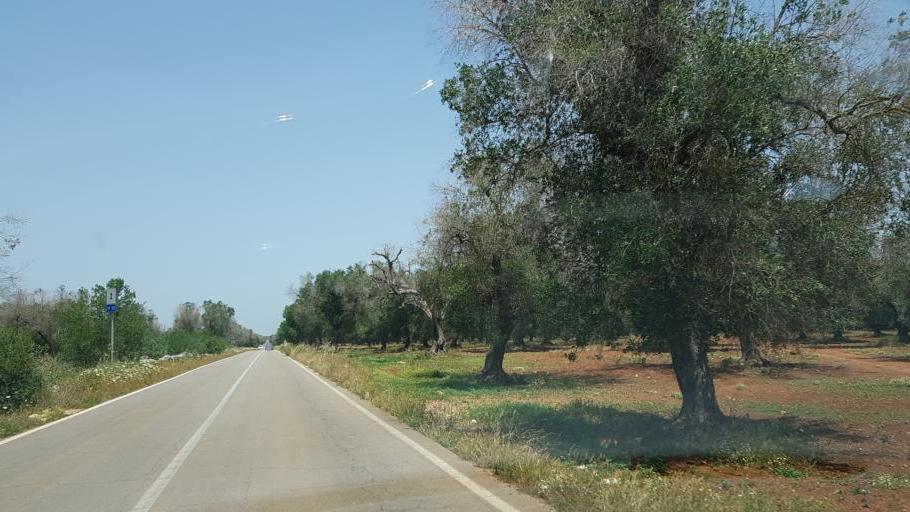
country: IT
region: Apulia
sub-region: Provincia di Lecce
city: Veglie
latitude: 40.3084
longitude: 17.9196
